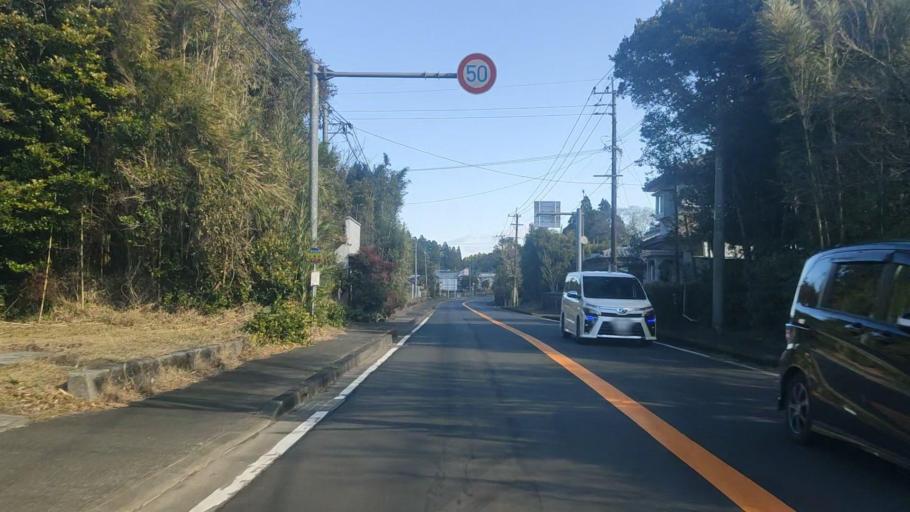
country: JP
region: Kagoshima
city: Sueyoshicho-ninokata
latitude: 31.6826
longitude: 130.9394
